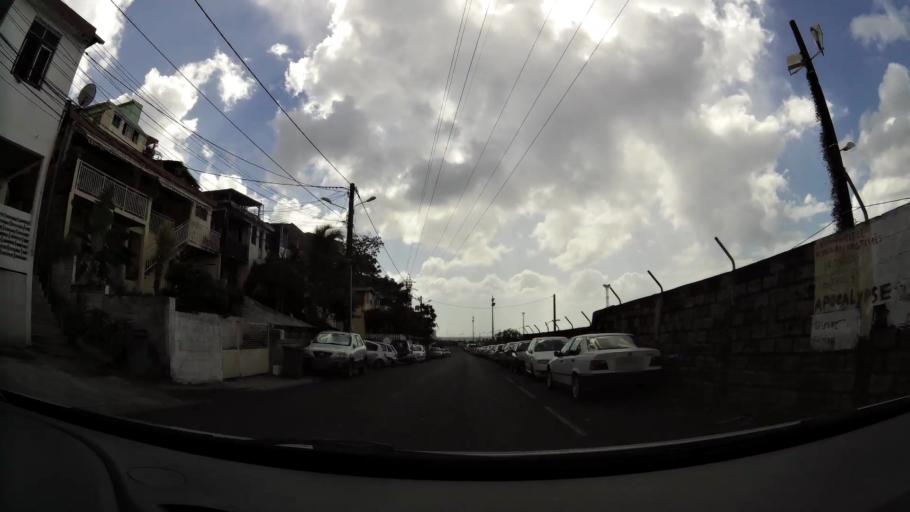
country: MQ
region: Martinique
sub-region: Martinique
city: Fort-de-France
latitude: 14.6001
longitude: -61.0577
